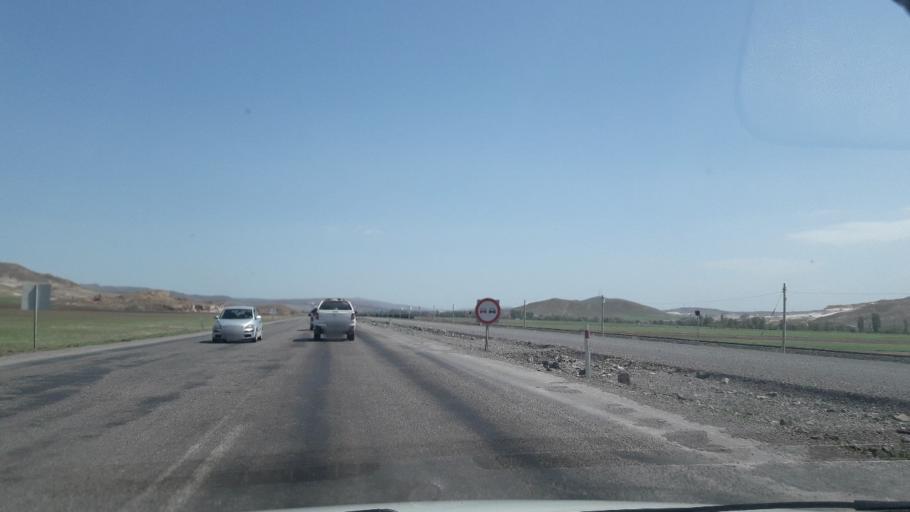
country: TR
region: Sivas
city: Ulas
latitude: 39.5297
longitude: 37.0147
